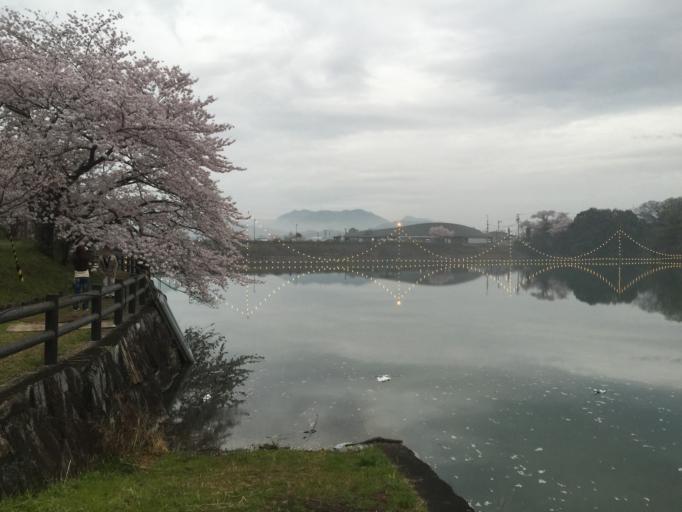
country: JP
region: Tokushima
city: Ikedacho
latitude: 34.1079
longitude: 133.7972
